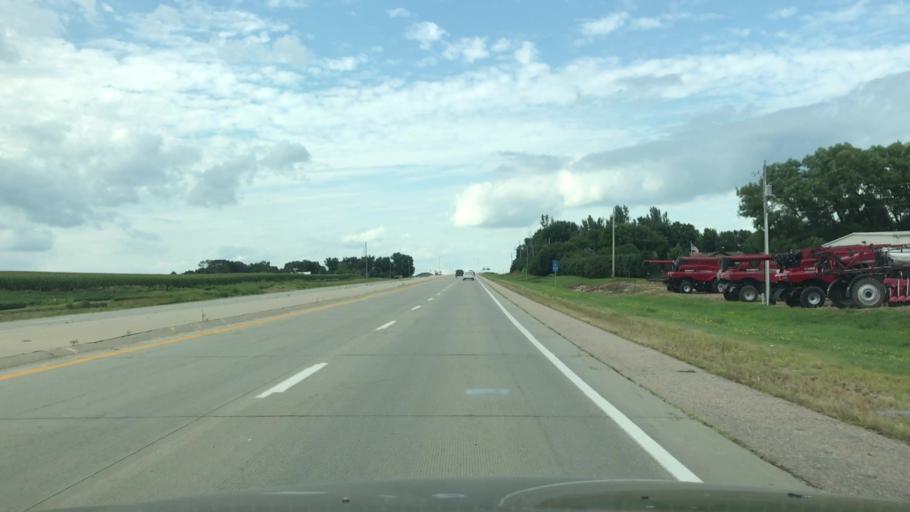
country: US
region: Iowa
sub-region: Plymouth County
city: Le Mars
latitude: 42.8102
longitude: -96.1747
